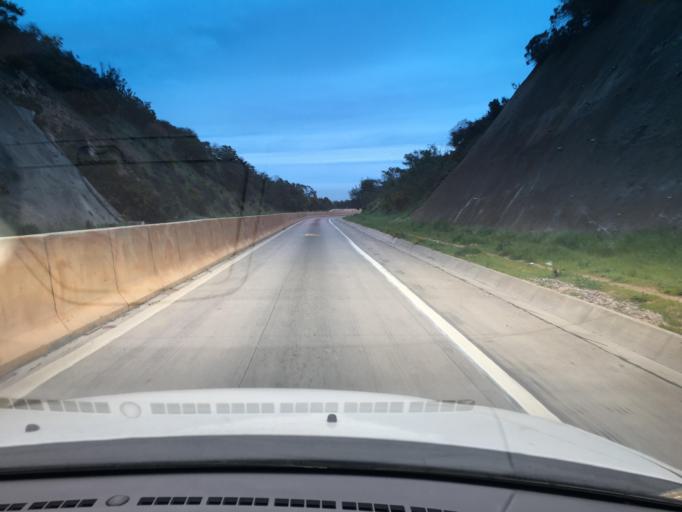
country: CL
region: Valparaiso
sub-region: Provincia de Valparaiso
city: Valparaiso
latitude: -33.0588
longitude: -71.6517
